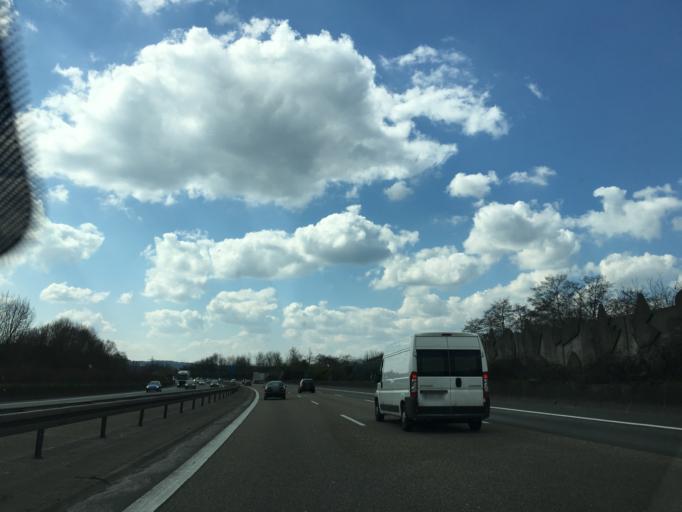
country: DE
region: North Rhine-Westphalia
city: Herdecke
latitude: 51.3968
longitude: 7.4478
